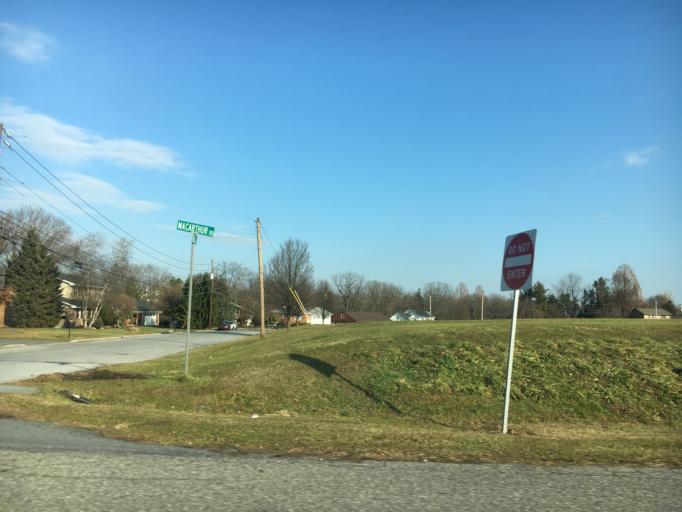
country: US
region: Pennsylvania
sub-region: Lehigh County
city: Stiles
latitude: 40.6591
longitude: -75.5081
